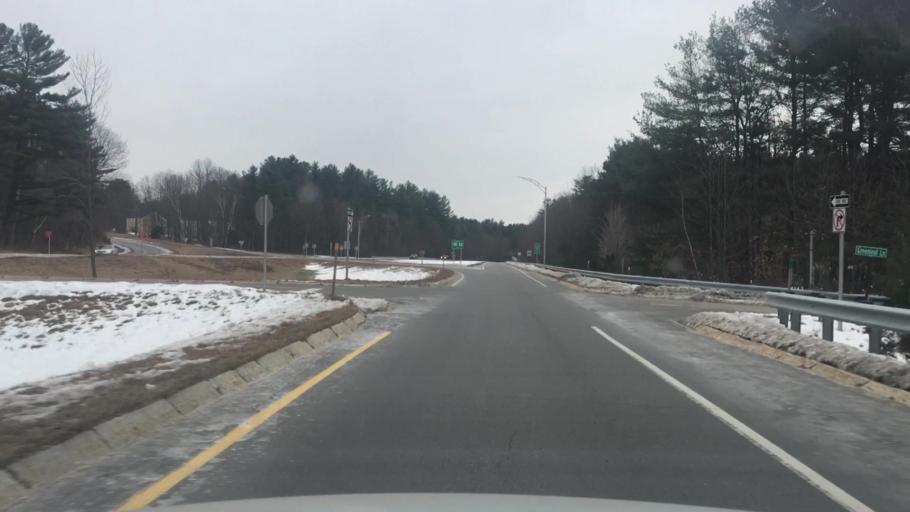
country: US
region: New Hampshire
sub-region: Merrimack County
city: Hopkinton
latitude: 43.1876
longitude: -71.6605
